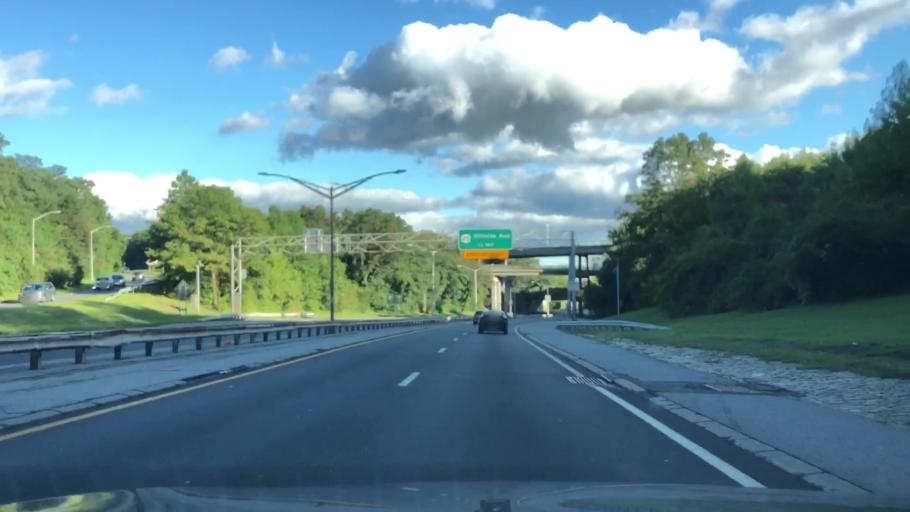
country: US
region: New York
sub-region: Nassau County
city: Bellerose Terrace
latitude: 40.7277
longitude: -73.7592
